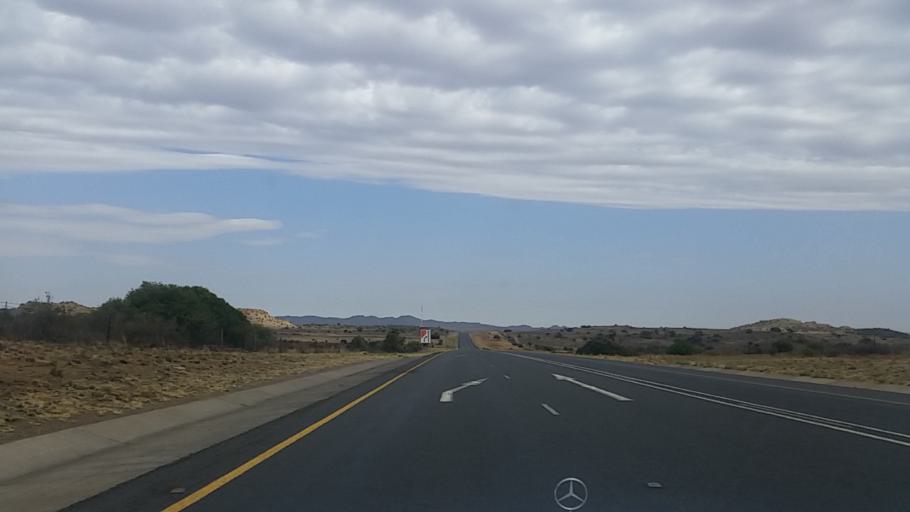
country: ZA
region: Northern Cape
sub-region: Pixley ka Seme District Municipality
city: Colesberg
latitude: -30.6191
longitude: 25.3247
